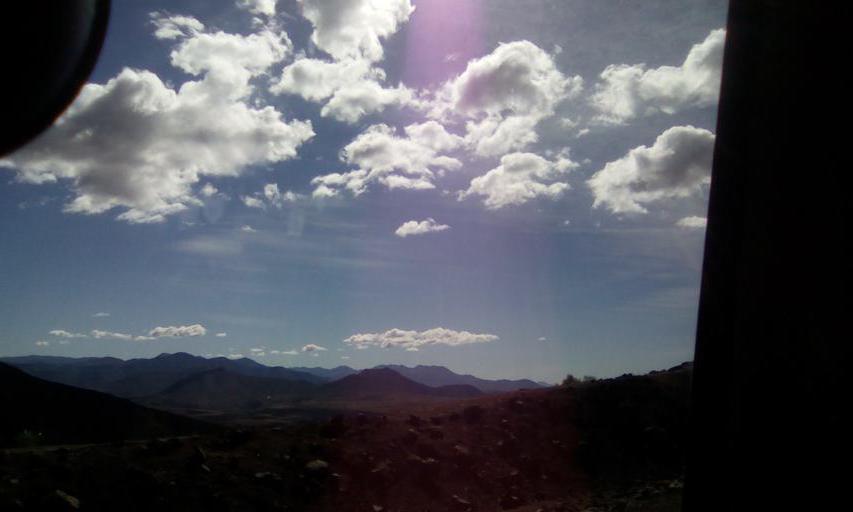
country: LS
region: Qacha's Nek
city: Qacha's Nek
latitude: -30.0090
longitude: 28.1669
